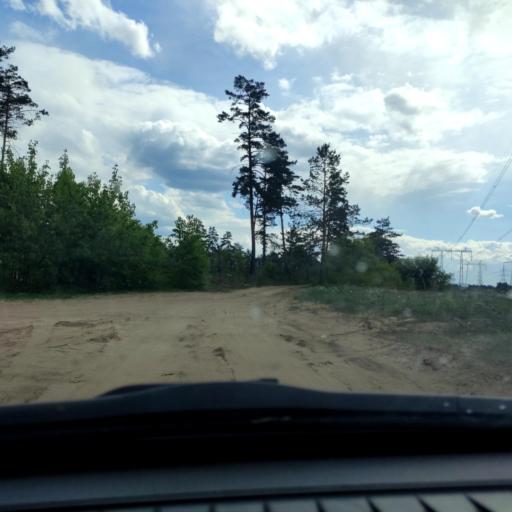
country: RU
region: Samara
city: Zhigulevsk
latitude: 53.5358
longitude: 49.5472
